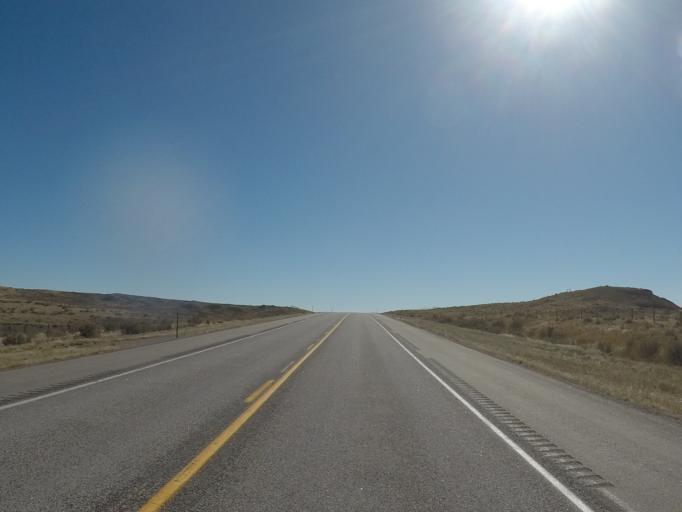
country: US
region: Montana
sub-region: Carbon County
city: Red Lodge
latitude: 44.9831
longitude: -109.0576
